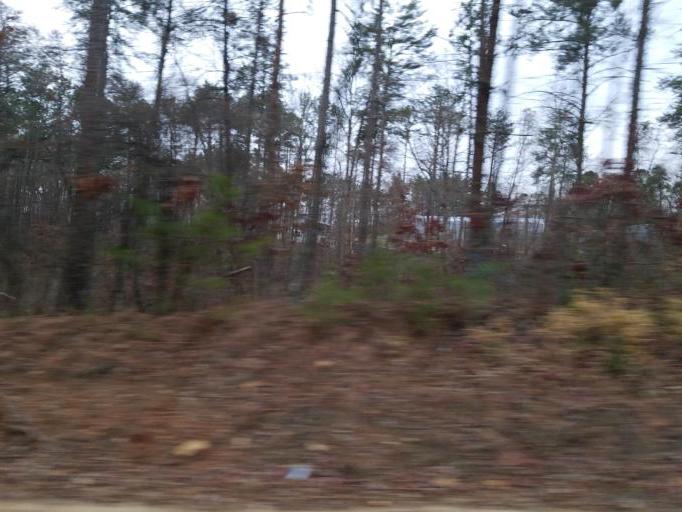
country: US
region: Georgia
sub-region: Dawson County
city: Dawsonville
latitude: 34.4526
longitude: -84.1310
